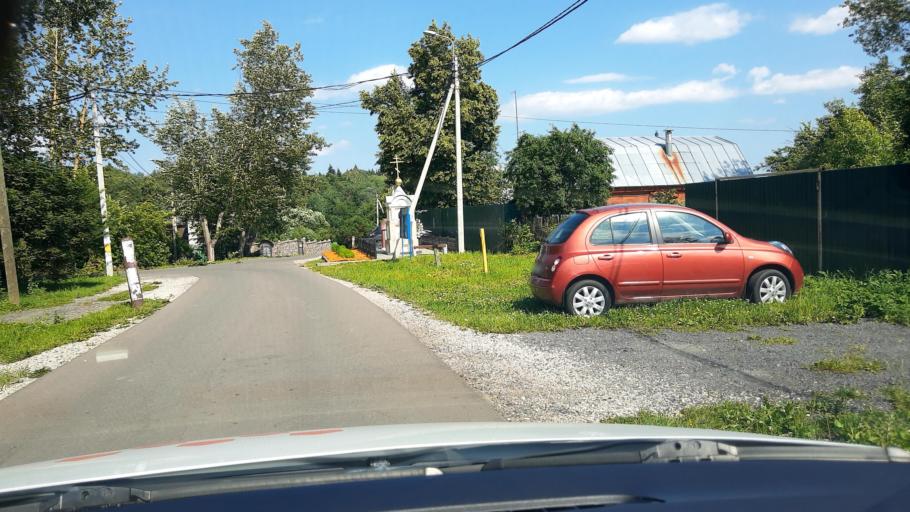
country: RU
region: Moscow
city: Vnukovo
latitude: 55.5580
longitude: 37.2103
